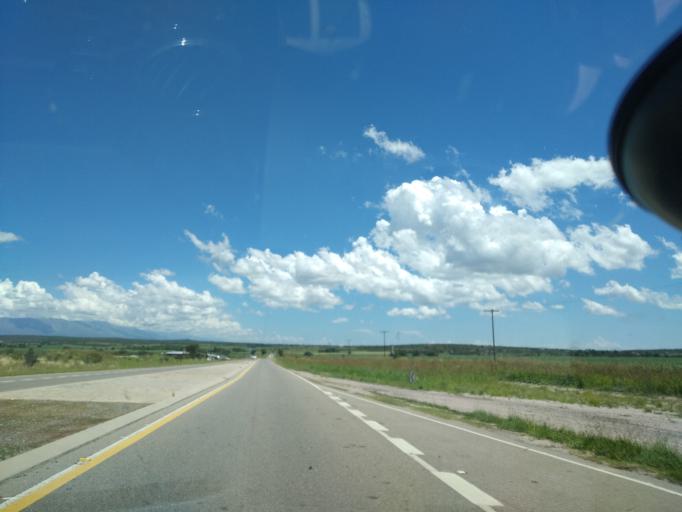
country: AR
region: Cordoba
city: Villa Cura Brochero
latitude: -31.6561
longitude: -65.0990
